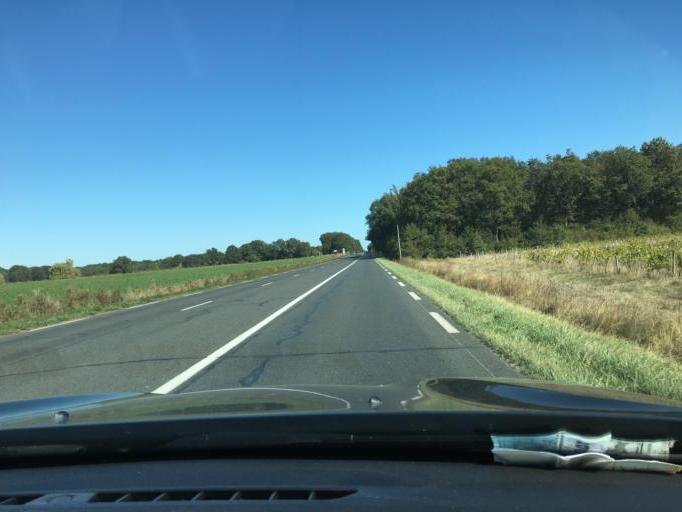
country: FR
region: Centre
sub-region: Departement d'Indre-et-Loire
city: Azay-le-Rideau
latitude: 47.2743
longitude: 0.4898
